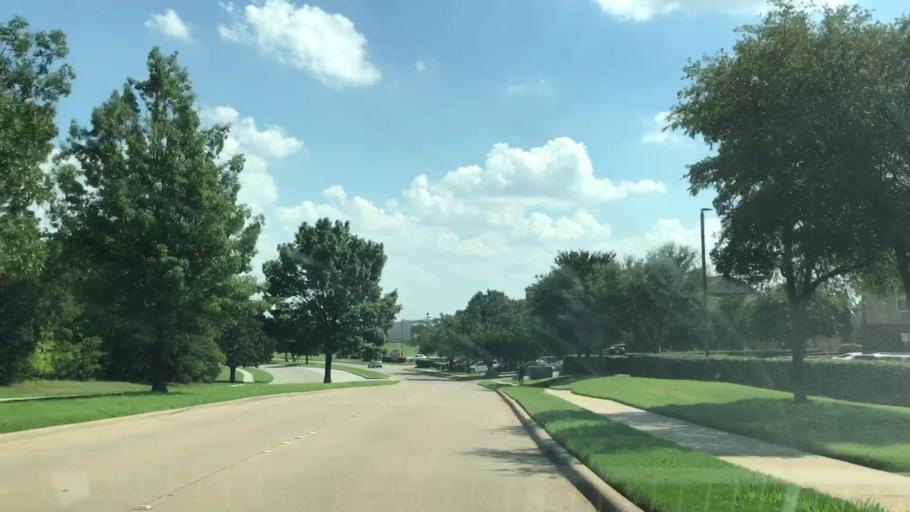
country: US
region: Texas
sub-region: Denton County
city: Lewisville
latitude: 33.0170
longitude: -96.9784
